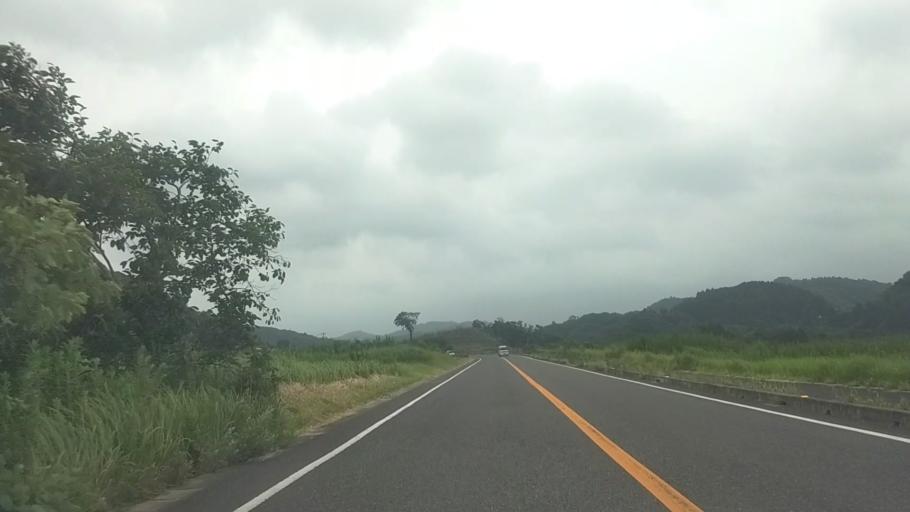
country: JP
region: Chiba
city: Kimitsu
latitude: 35.2194
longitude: 139.9397
